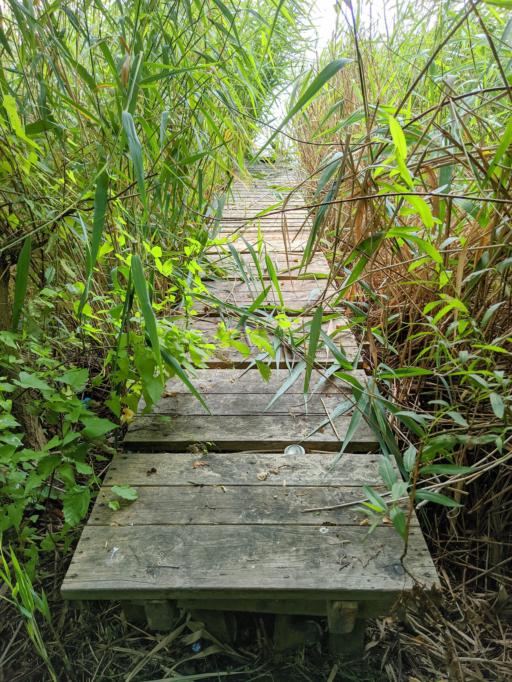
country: PL
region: Lubusz
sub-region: Powiat swiebodzinski
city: Lubrza
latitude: 52.2525
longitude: 15.4674
